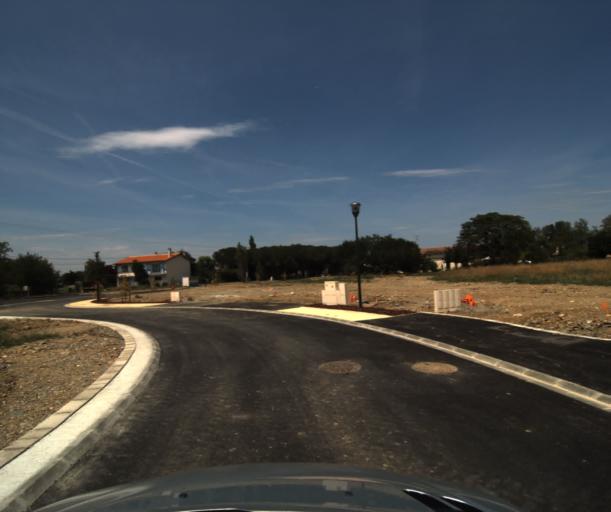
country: FR
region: Midi-Pyrenees
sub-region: Departement de la Haute-Garonne
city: Labastidette
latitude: 43.4617
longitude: 1.2440
